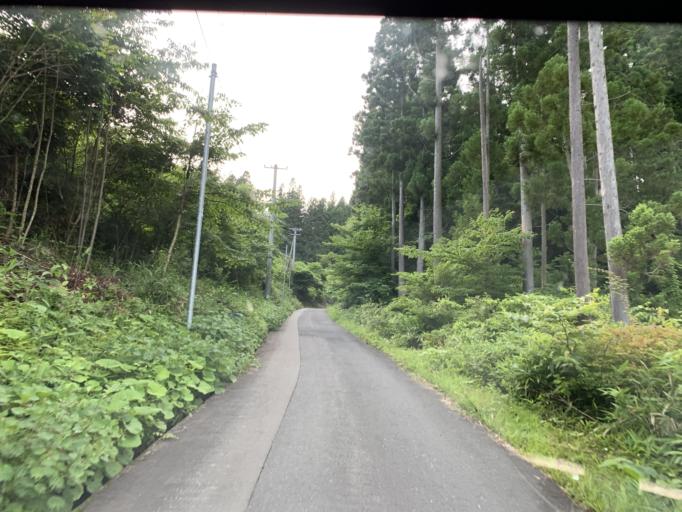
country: JP
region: Iwate
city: Ichinoseki
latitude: 38.8975
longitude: 141.0134
